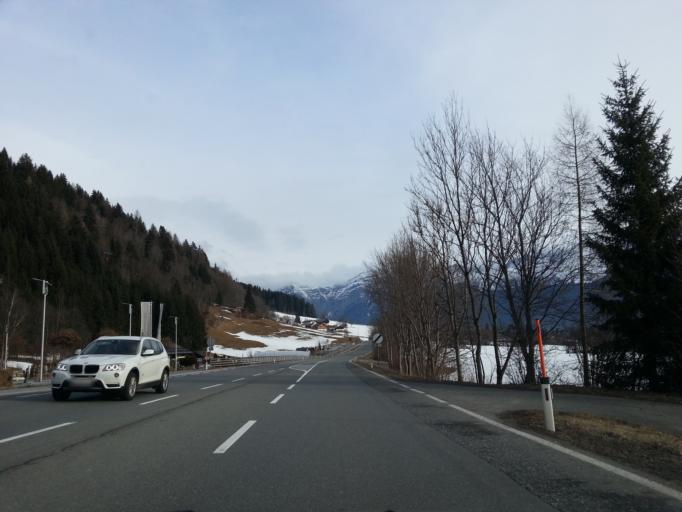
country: AT
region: Salzburg
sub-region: Politischer Bezirk Zell am See
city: Maishofen
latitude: 47.4066
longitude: 12.8086
